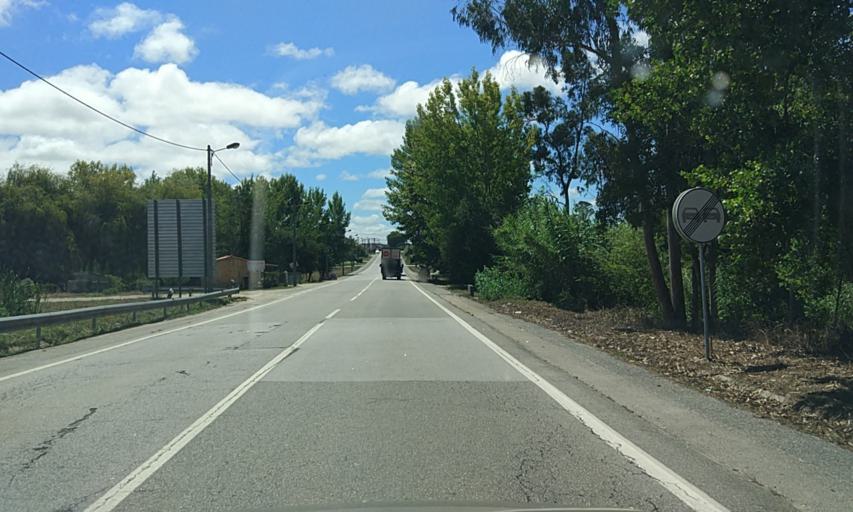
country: PT
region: Aveiro
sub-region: Vagos
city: Vagos
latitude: 40.5007
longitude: -8.6816
